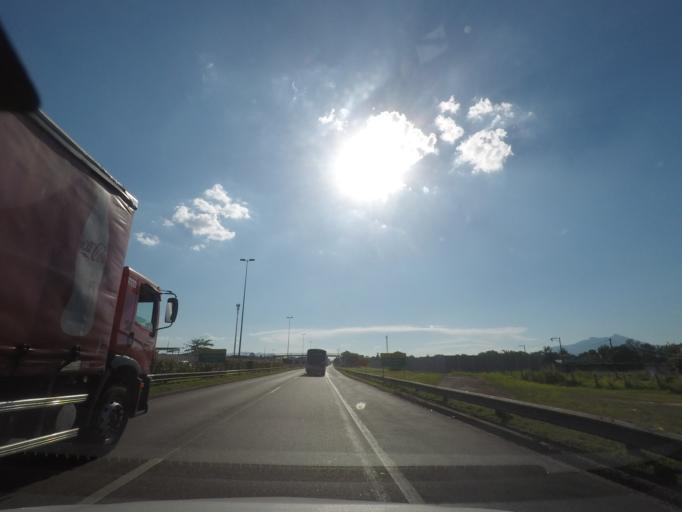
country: BR
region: Rio de Janeiro
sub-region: Duque De Caxias
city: Duque de Caxias
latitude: -22.6670
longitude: -43.2644
